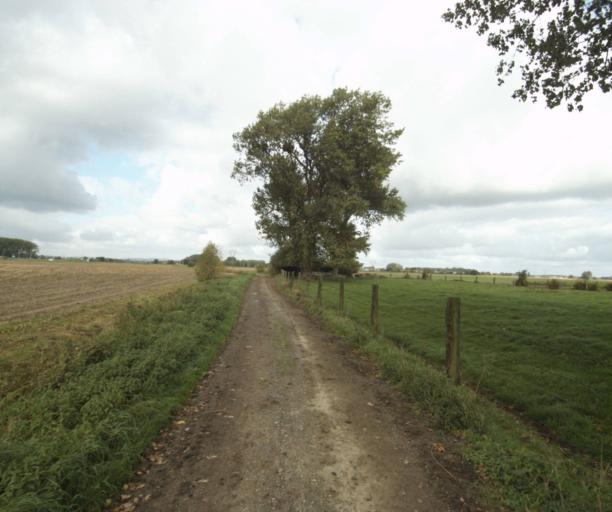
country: FR
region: Nord-Pas-de-Calais
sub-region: Departement du Nord
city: Frelinghien
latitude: 50.6971
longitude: 2.9358
